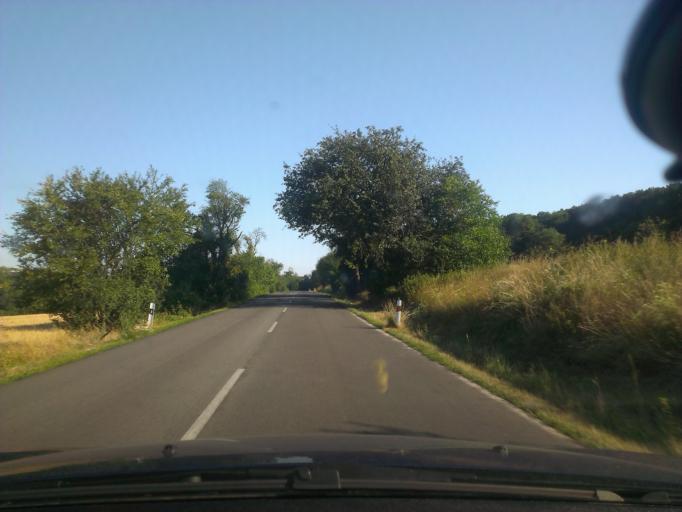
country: SK
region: Trnavsky
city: Vrbove
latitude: 48.6658
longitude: 17.6934
